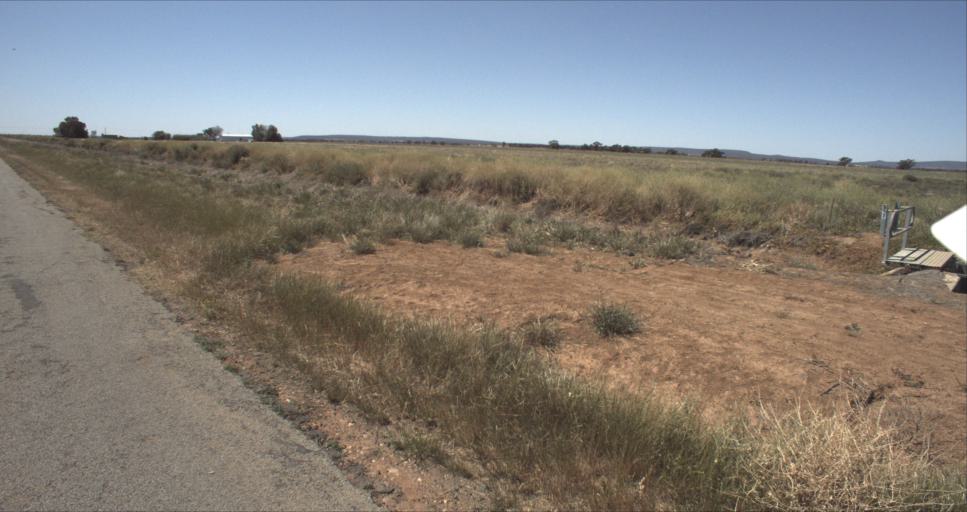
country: AU
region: New South Wales
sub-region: Leeton
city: Leeton
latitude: -34.5091
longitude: 146.3447
